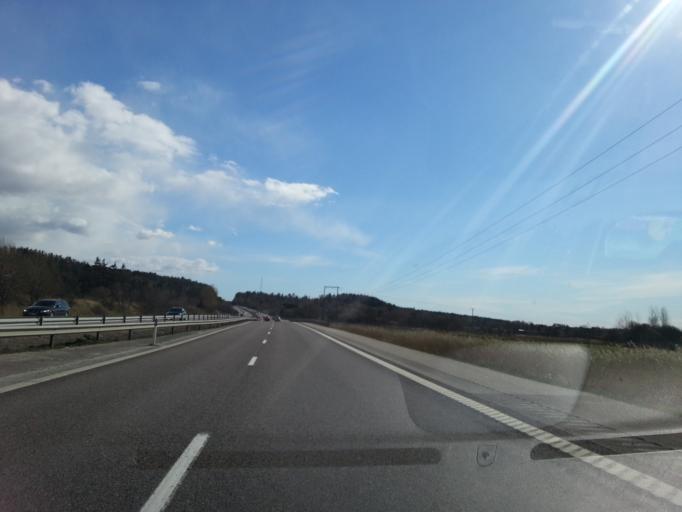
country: SE
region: Vaestra Goetaland
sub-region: Stenungsunds Kommun
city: Stora Hoga
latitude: 58.0156
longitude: 11.8433
